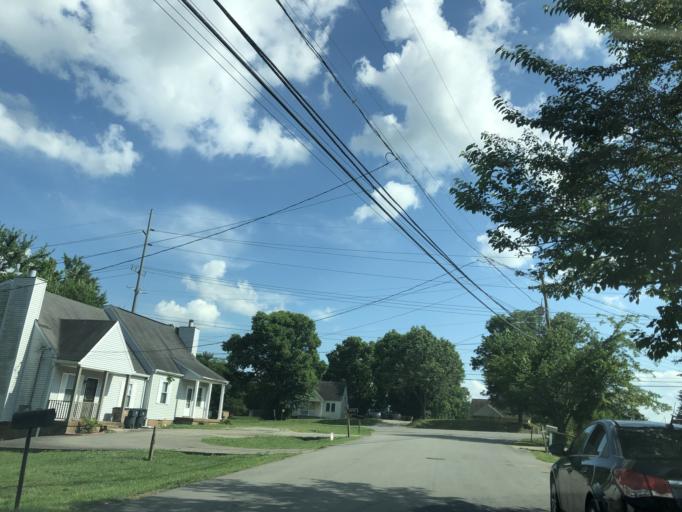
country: US
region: Tennessee
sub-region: Davidson County
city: Nashville
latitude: 36.2377
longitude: -86.8074
